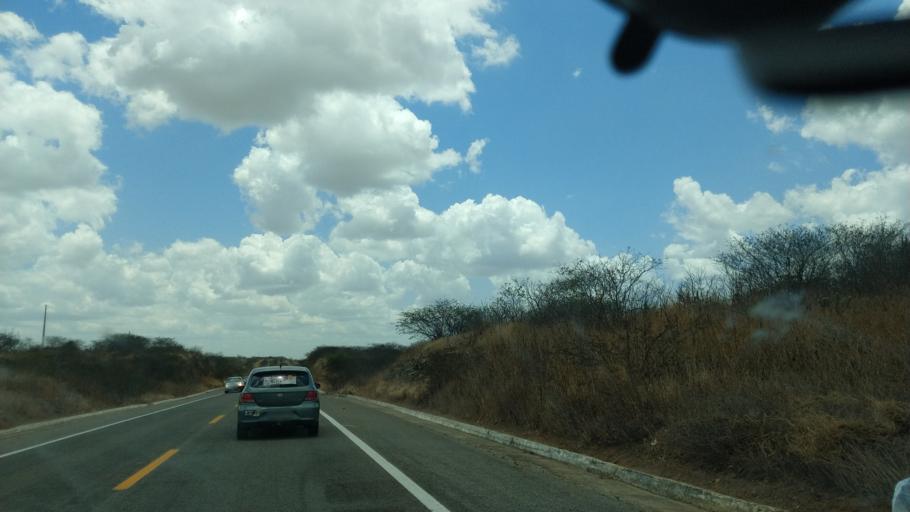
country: BR
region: Rio Grande do Norte
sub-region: Cerro Cora
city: Cerro Cora
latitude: -6.2098
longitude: -36.2956
